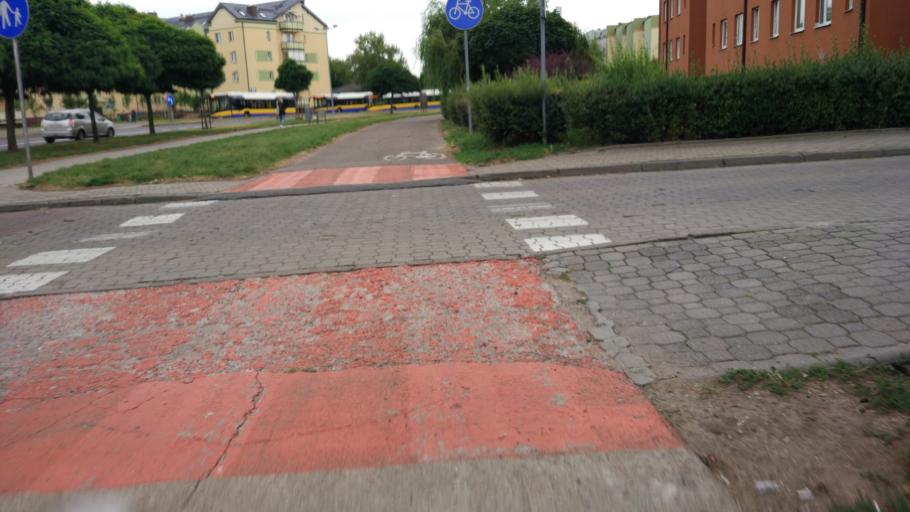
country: PL
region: Masovian Voivodeship
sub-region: Plock
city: Plock
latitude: 52.5314
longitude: 19.7591
